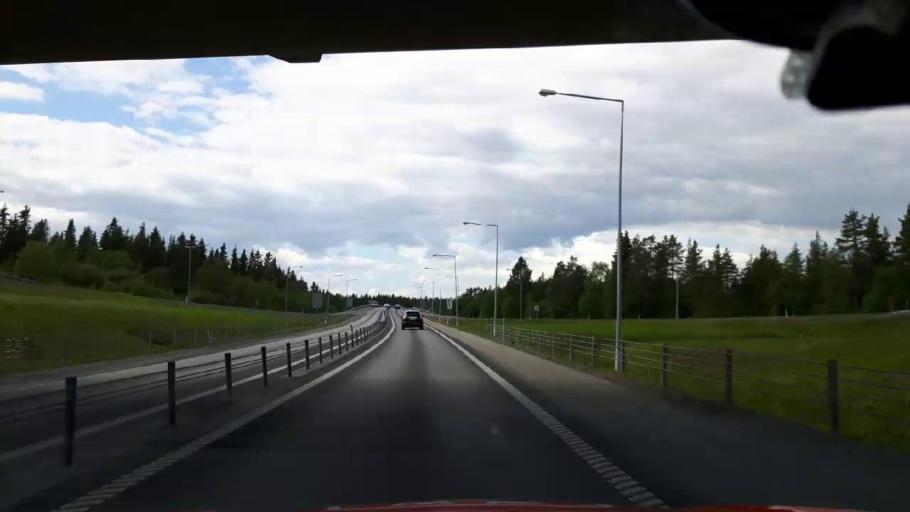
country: SE
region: Jaemtland
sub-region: OEstersunds Kommun
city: Ostersund
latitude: 63.2143
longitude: 14.6488
